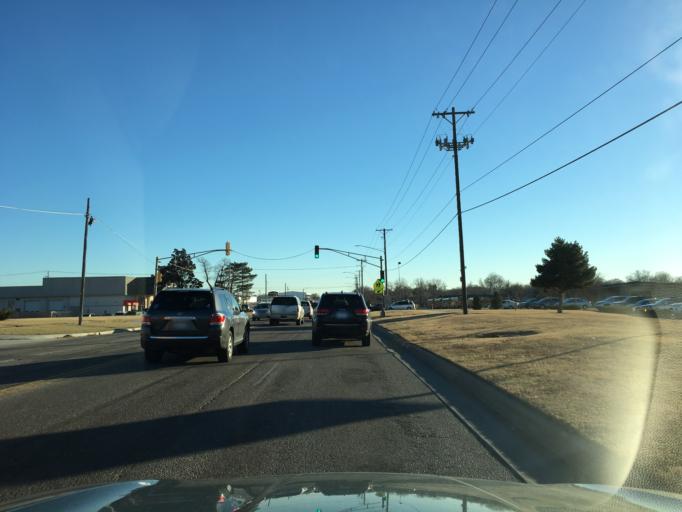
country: US
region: Kansas
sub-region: Sedgwick County
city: Bellaire
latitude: 37.6976
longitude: -97.2263
